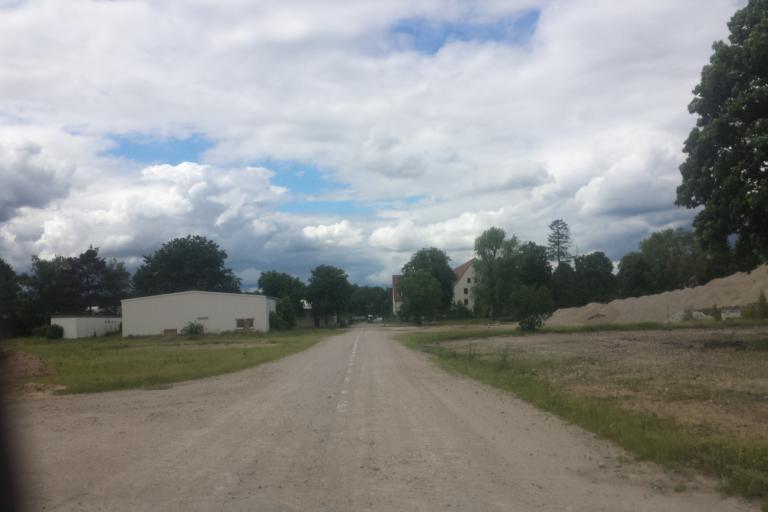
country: DE
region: Hesse
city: Viernheim
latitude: 49.5162
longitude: 8.5505
